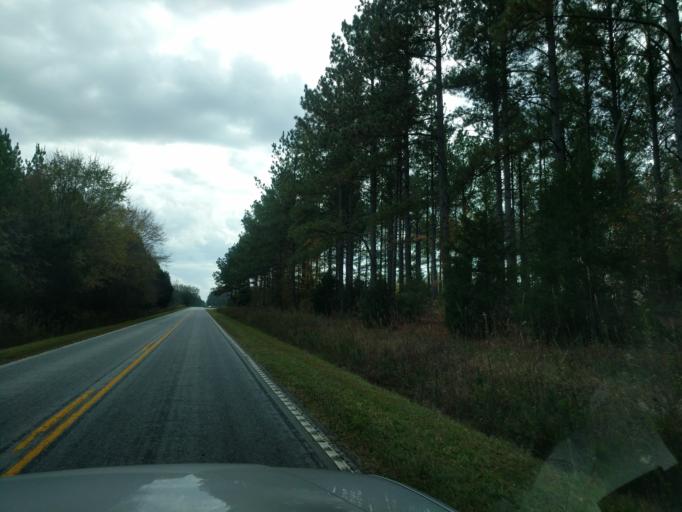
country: US
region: South Carolina
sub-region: Laurens County
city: Joanna
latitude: 34.4137
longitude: -81.8649
